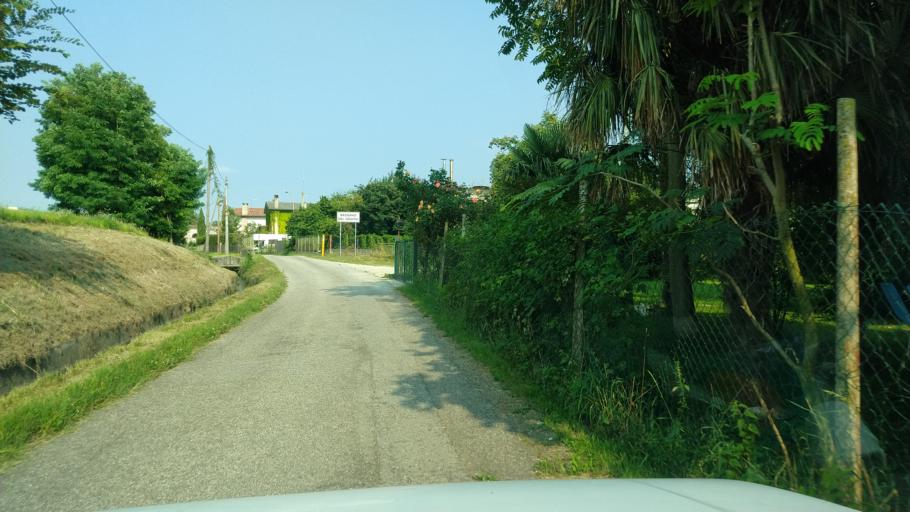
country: IT
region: Veneto
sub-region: Provincia di Vicenza
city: Nove
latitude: 45.7378
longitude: 11.6878
